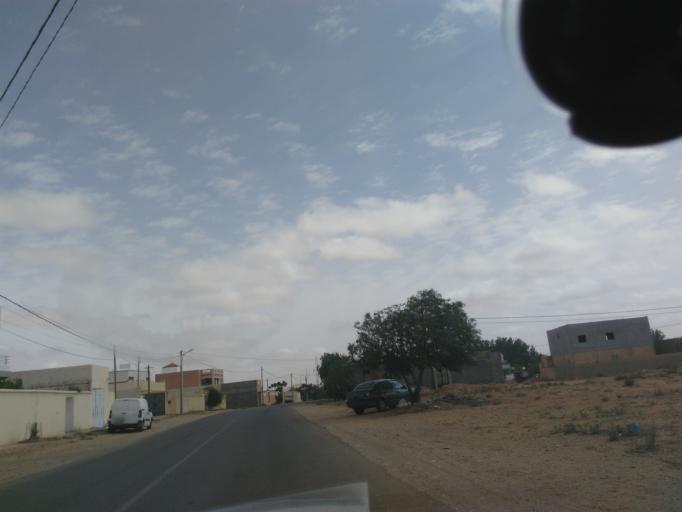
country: TN
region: Tataouine
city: Tataouine
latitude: 32.9548
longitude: 10.4650
